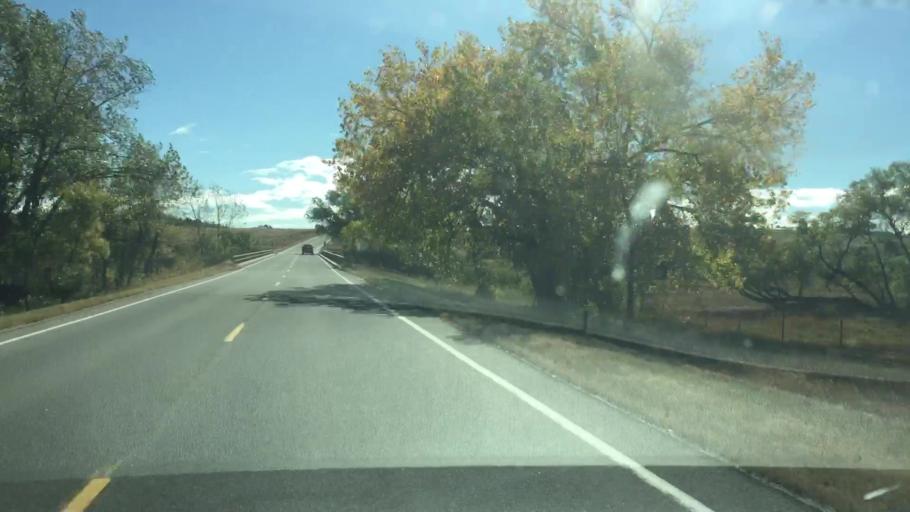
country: US
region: Colorado
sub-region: Elbert County
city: Kiowa
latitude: 39.3201
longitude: -104.3806
